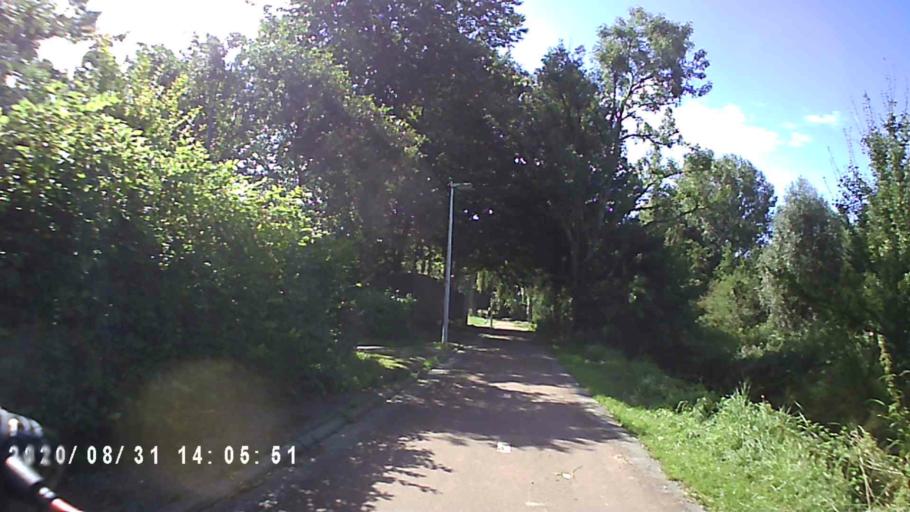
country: NL
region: Groningen
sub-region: Gemeente Zuidhorn
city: Aduard
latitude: 53.2050
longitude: 6.4986
